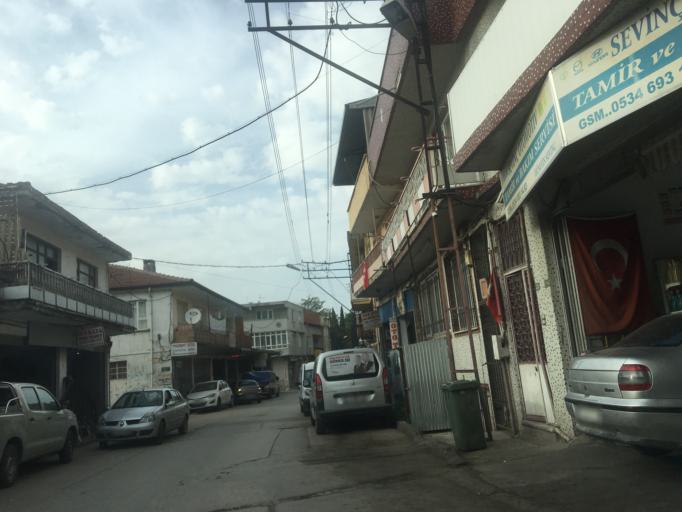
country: TR
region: Bursa
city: Yildirim
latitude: 40.2010
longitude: 29.0456
